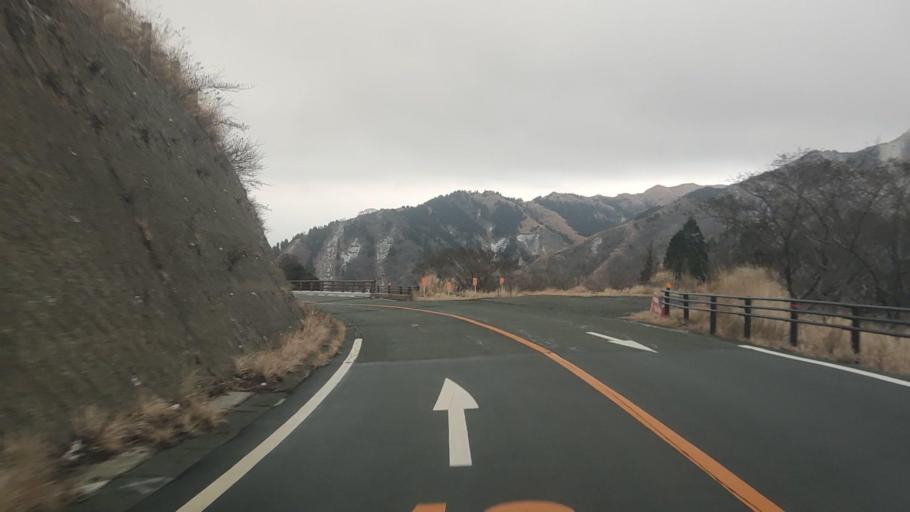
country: JP
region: Kumamoto
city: Aso
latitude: 32.8708
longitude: 131.0676
